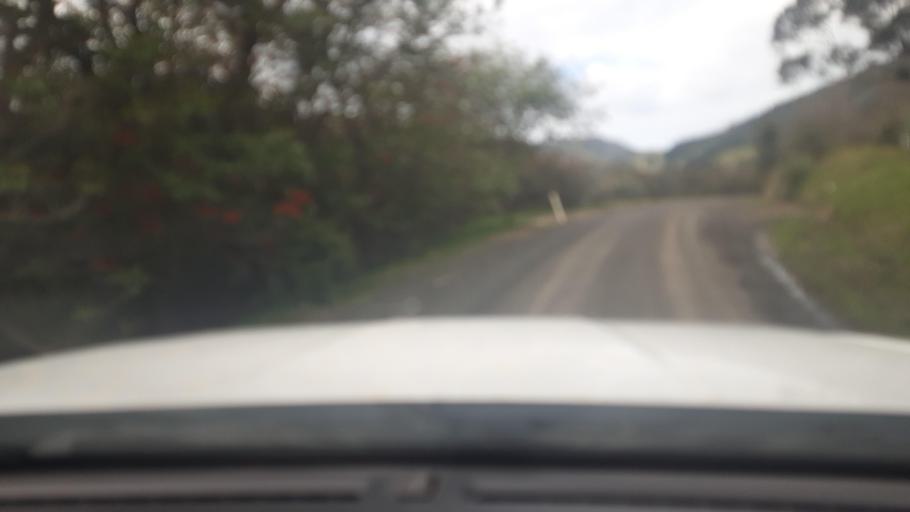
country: NZ
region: Northland
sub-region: Far North District
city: Ahipara
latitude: -35.3326
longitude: 173.2266
